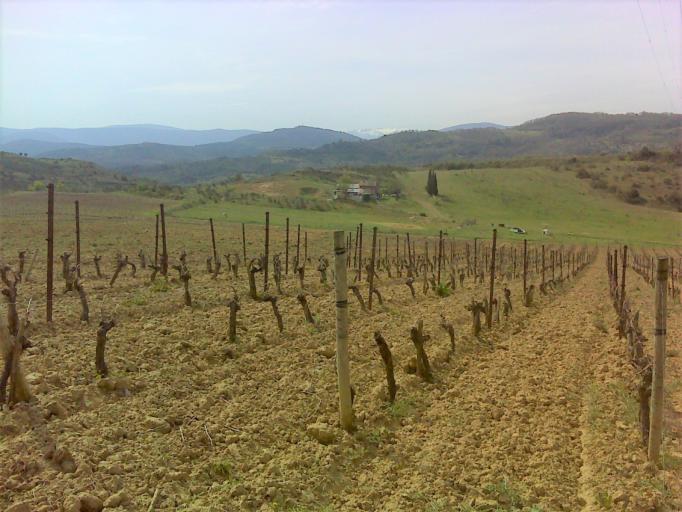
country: FR
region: Languedoc-Roussillon
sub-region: Departement de l'Aude
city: Esperaza
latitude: 42.9424
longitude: 2.2047
